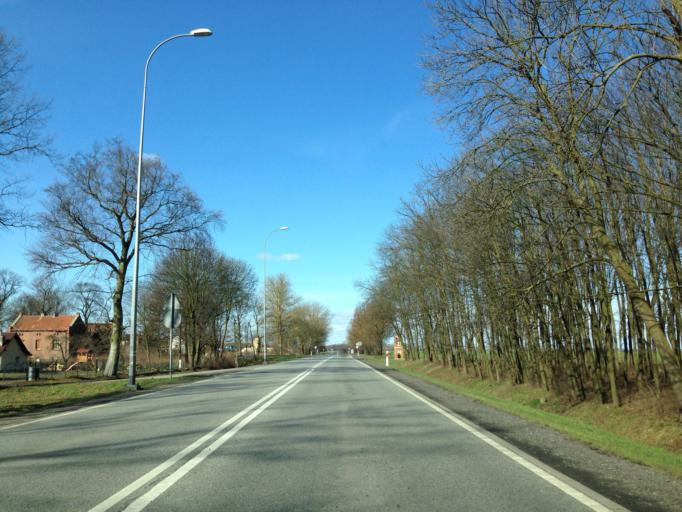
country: PL
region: Pomeranian Voivodeship
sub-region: Powiat malborski
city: Miloradz
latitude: 54.0540
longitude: 18.9123
